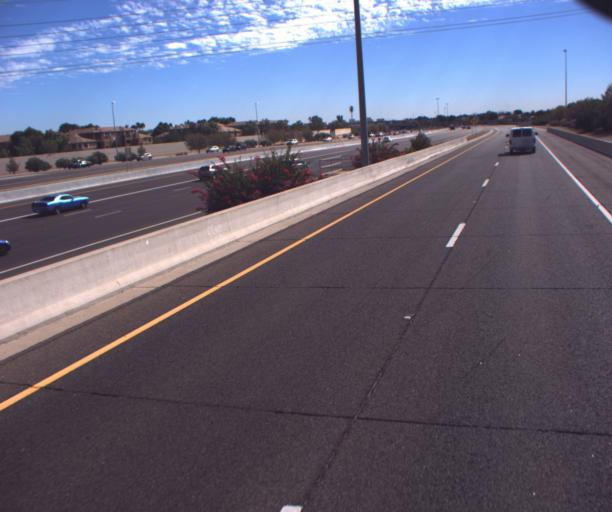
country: US
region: Arizona
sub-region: Maricopa County
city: Chandler
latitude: 33.2896
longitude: -111.8855
